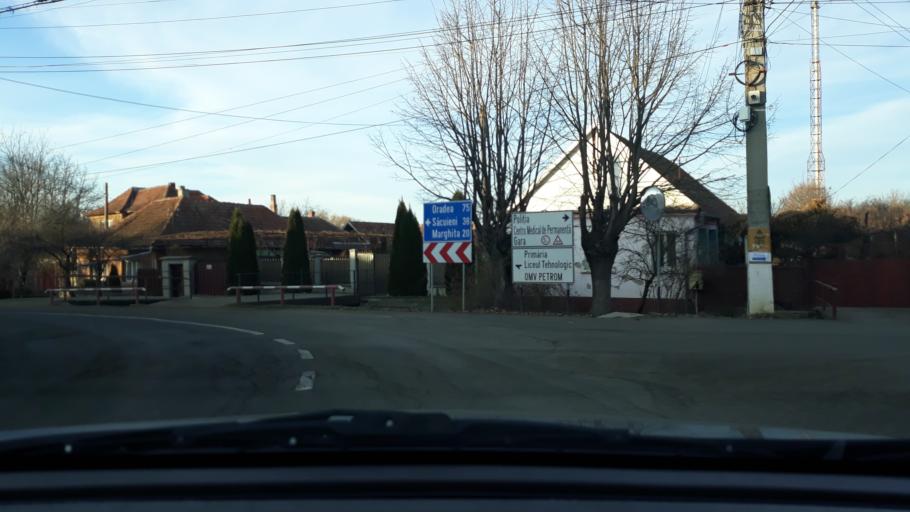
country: RO
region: Bihor
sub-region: Comuna Suplacu de Barcau
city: Suplacu de Barcau
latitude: 47.2572
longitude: 22.5315
